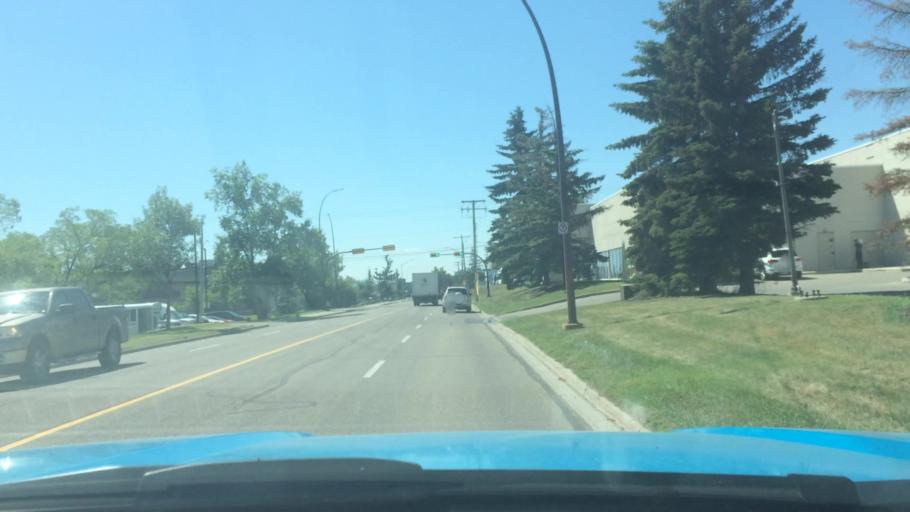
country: CA
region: Alberta
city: Calgary
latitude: 51.0533
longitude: -113.9934
